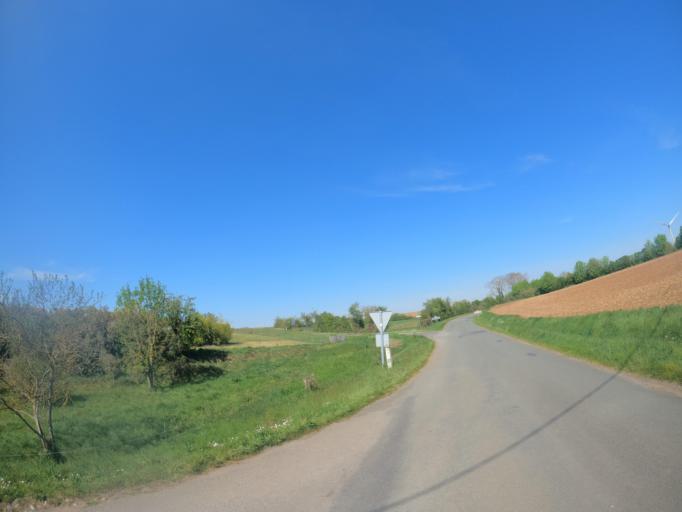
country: FR
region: Poitou-Charentes
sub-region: Departement des Deux-Sevres
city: Airvault
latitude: 46.8852
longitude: -0.1327
